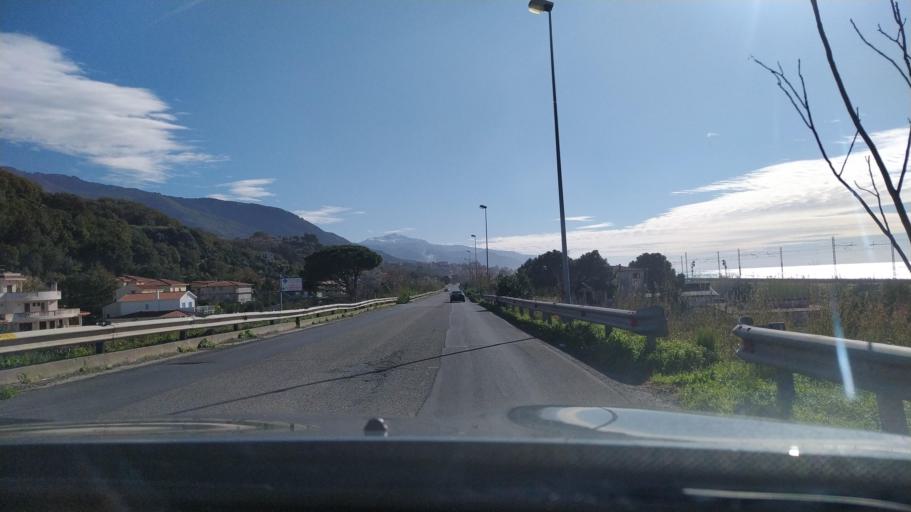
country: IT
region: Calabria
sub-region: Provincia di Cosenza
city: Scarcelli
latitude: 39.3838
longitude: 16.0224
